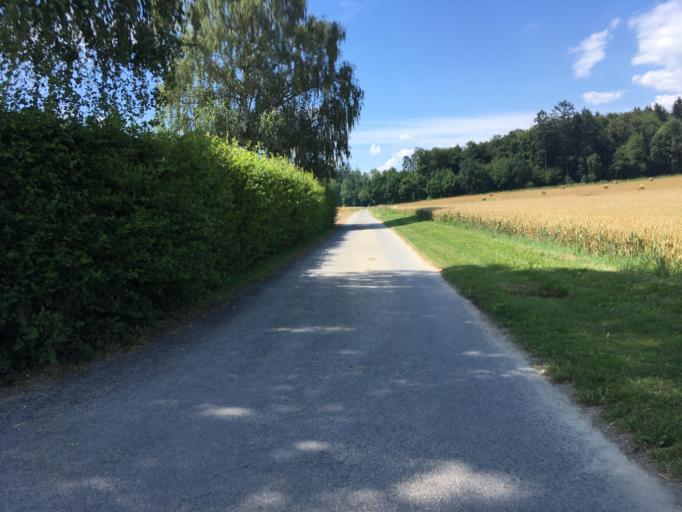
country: CH
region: Fribourg
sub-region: Broye District
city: Domdidier
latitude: 46.9376
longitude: 6.9967
